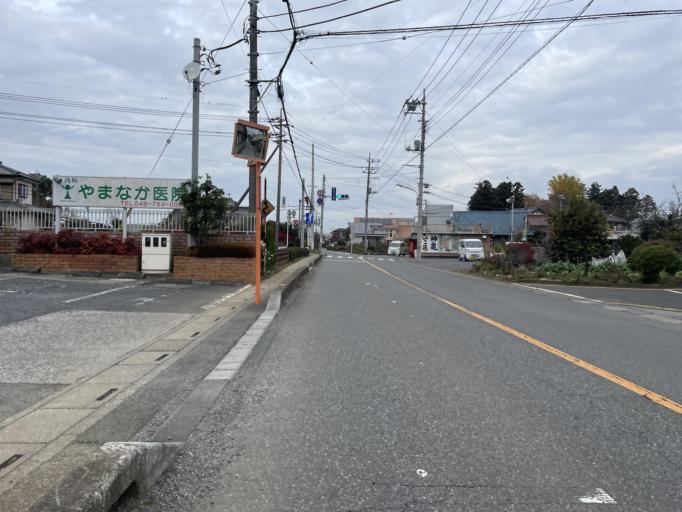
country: JP
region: Saitama
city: Shiraoka
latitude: 36.0053
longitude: 139.6615
